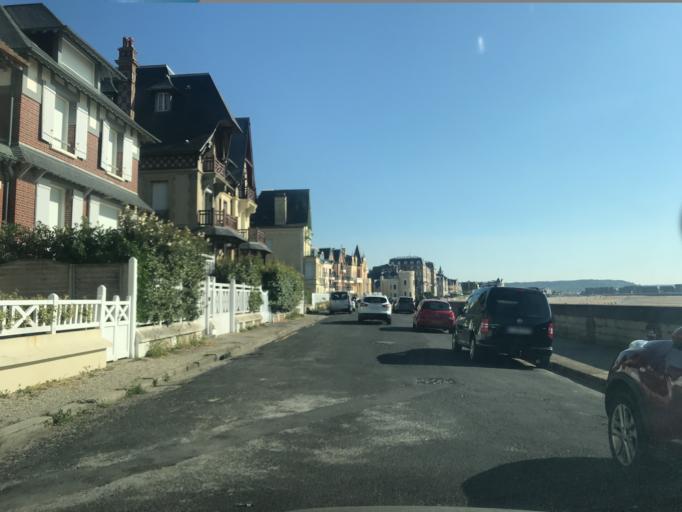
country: FR
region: Lower Normandy
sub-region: Departement du Calvados
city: Trouville-sur-Mer
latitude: 49.3754
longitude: 0.0860
